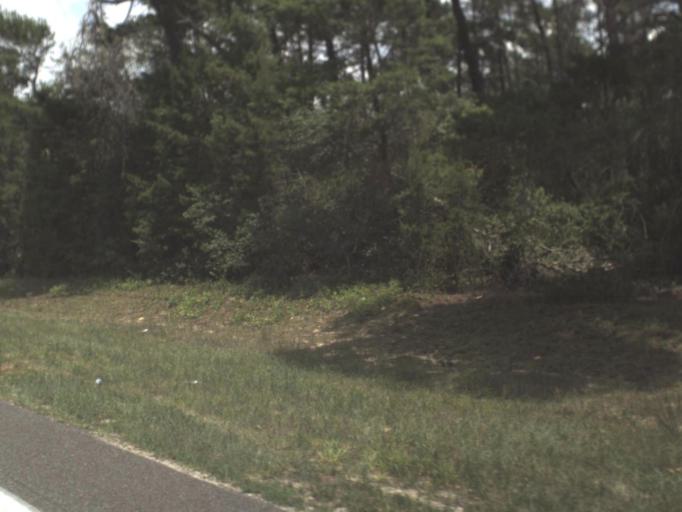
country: US
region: Florida
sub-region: Putnam County
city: Crescent City
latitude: 29.4003
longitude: -81.7367
